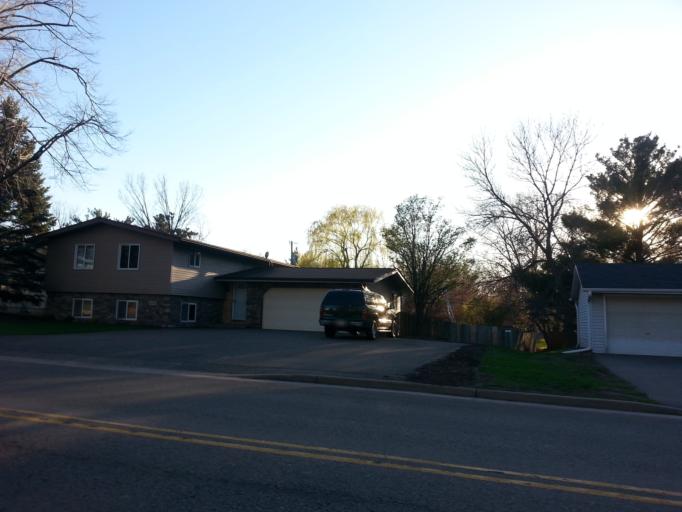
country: US
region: Wisconsin
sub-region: Saint Croix County
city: Hudson
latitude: 44.9649
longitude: -92.7436
